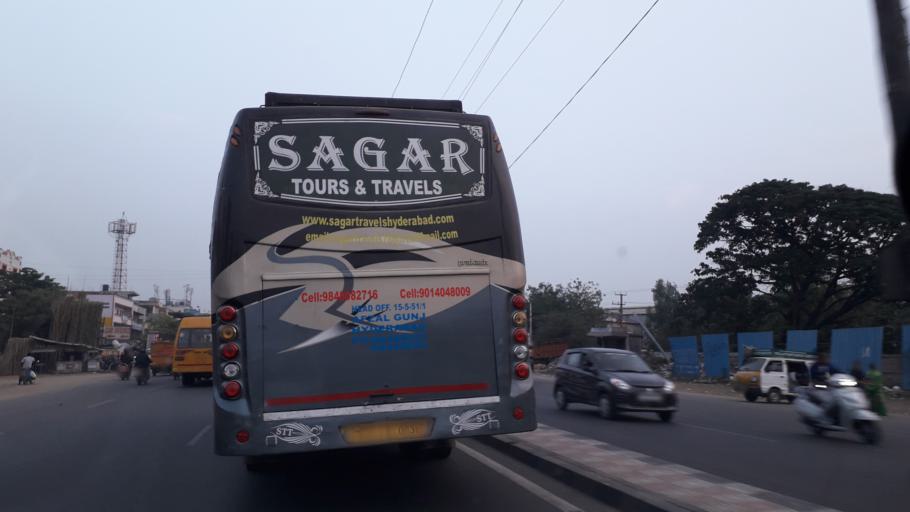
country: IN
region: Telangana
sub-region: Medak
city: Serilingampalle
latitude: 17.5056
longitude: 78.3065
